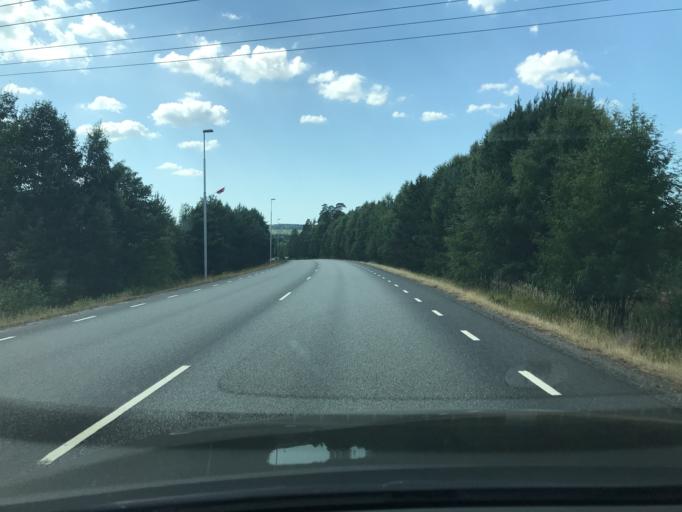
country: SE
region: Skane
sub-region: Hassleholms Kommun
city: Hastveda
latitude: 56.2757
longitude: 13.9462
